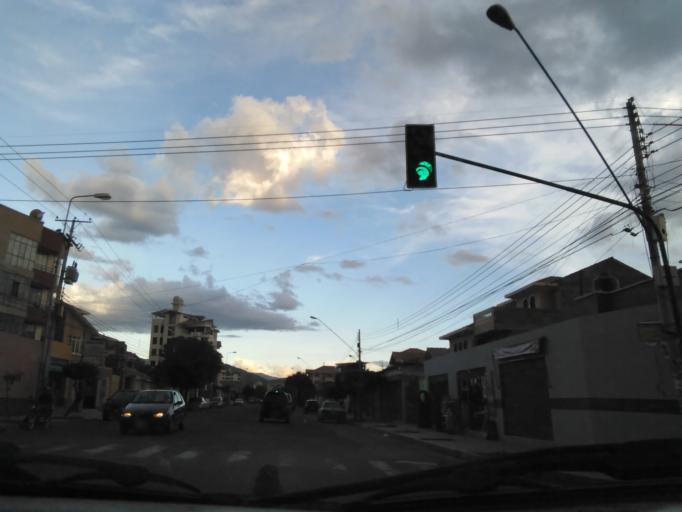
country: BO
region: Cochabamba
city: Cochabamba
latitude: -17.3880
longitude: -66.1778
